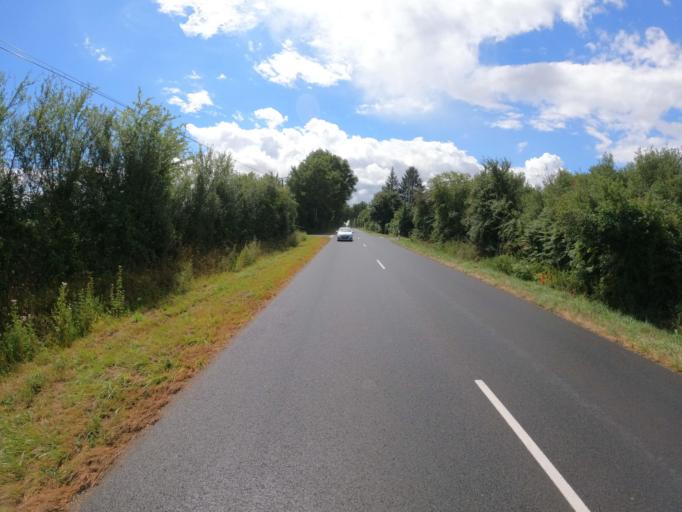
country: FR
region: Pays de la Loire
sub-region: Departement de Maine-et-Loire
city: Feneu
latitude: 47.5956
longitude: -0.5887
